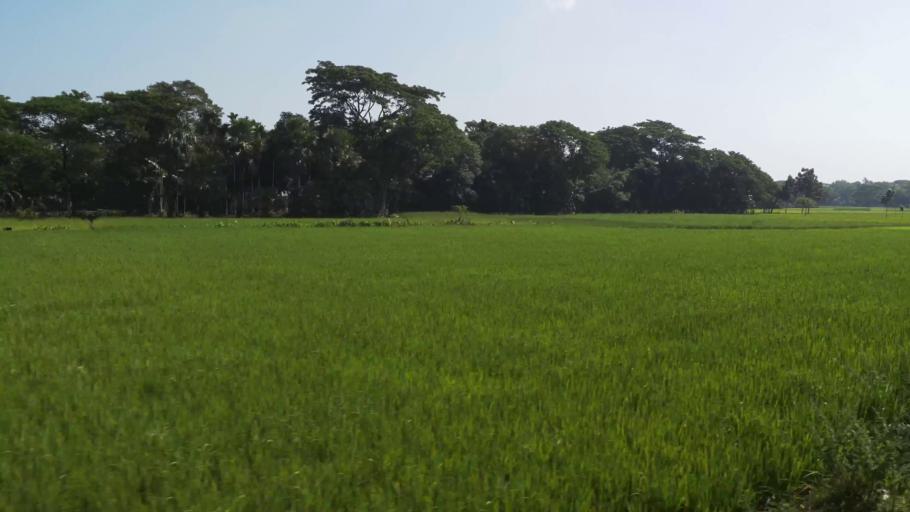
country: BD
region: Dhaka
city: Gafargaon
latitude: 24.5139
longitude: 90.5127
